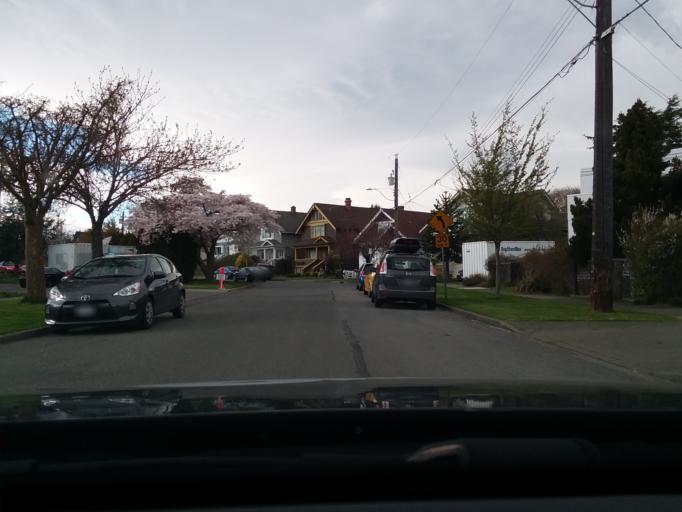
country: CA
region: British Columbia
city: Victoria
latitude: 48.4157
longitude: -123.3465
